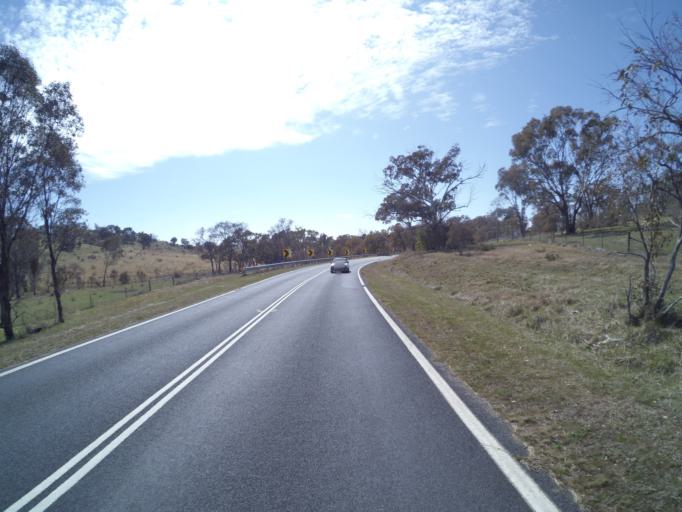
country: AU
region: Australian Capital Territory
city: Macarthur
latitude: -35.4496
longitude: 149.0474
